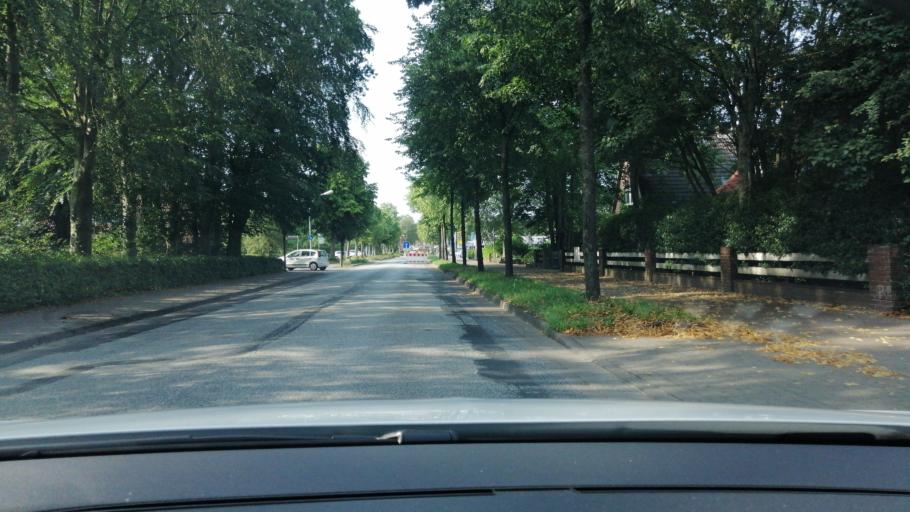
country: DE
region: Schleswig-Holstein
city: Leck
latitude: 54.7687
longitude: 8.9772
